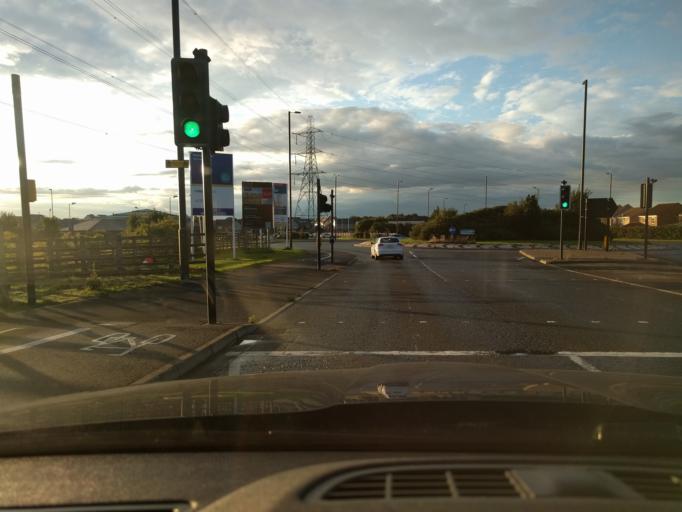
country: GB
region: England
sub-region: Northumberland
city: Backworth
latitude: 55.0337
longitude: -1.5227
